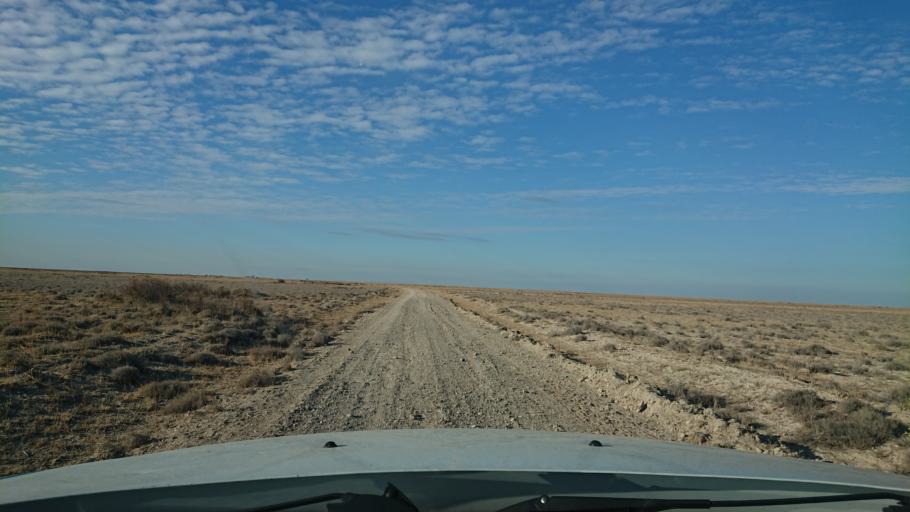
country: TR
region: Aksaray
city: Eskil
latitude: 38.5502
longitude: 33.3164
